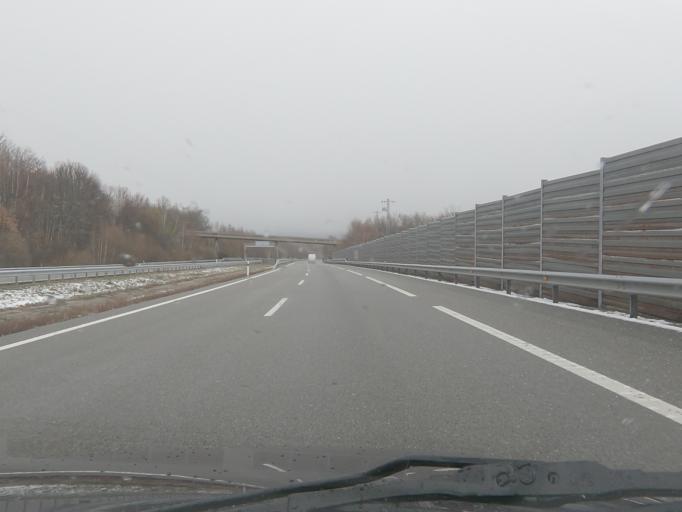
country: ES
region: Castille and Leon
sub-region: Provincia de Zamora
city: Requejo
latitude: 42.0355
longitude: -6.7286
